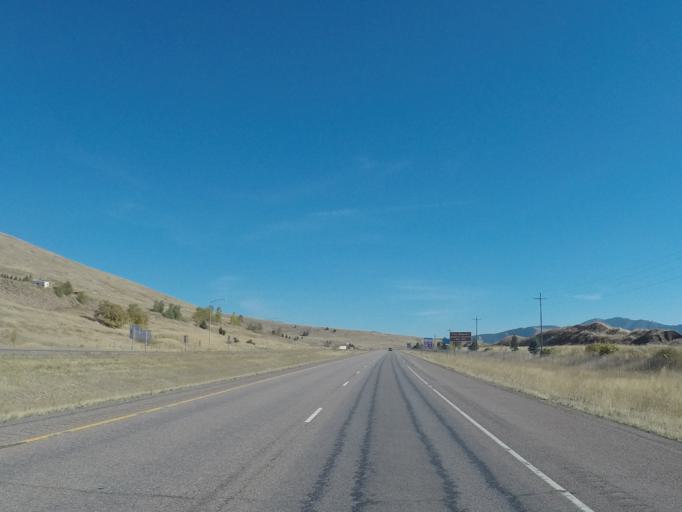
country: US
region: Montana
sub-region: Missoula County
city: Orchard Homes
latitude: 46.9178
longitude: -114.0493
